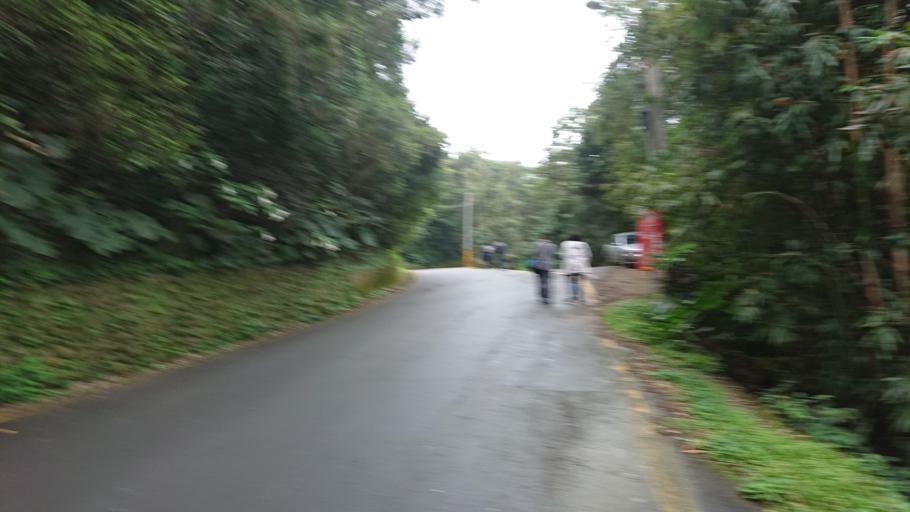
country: TW
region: Taiwan
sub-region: Taoyuan
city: Taoyuan
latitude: 24.9326
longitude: 121.3656
